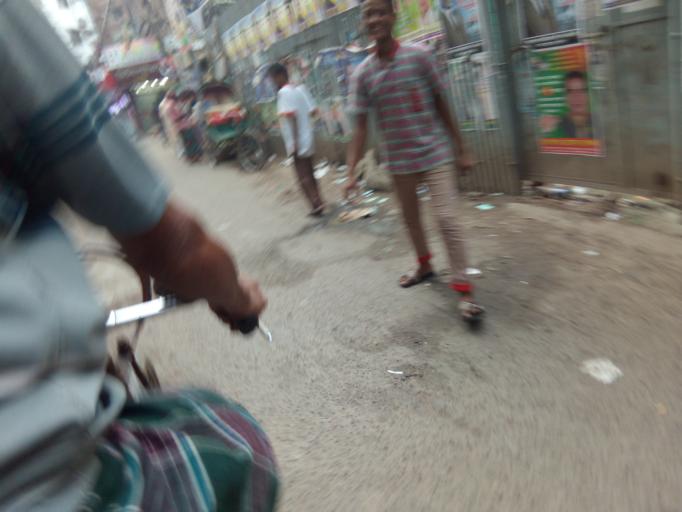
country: BD
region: Dhaka
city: Azimpur
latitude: 23.7195
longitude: 90.3905
